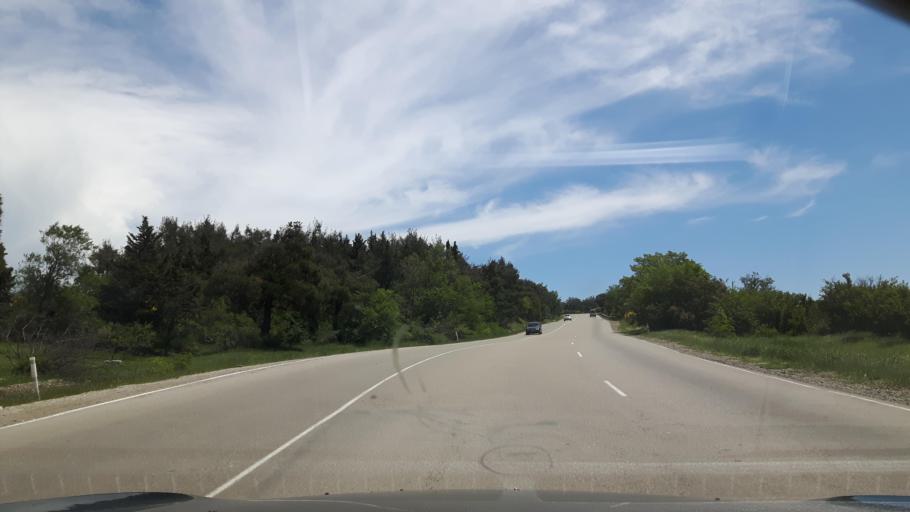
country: GE
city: Didi Lilo
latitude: 41.6935
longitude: 45.0825
